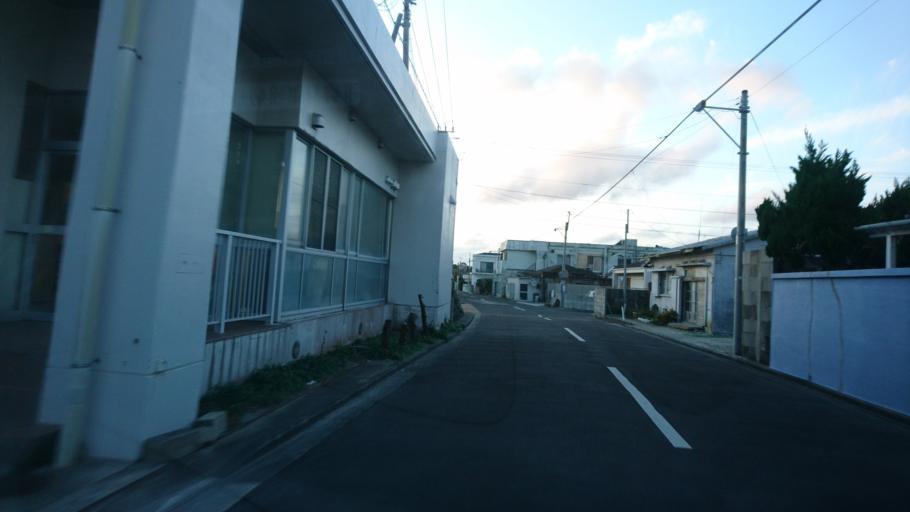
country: JP
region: Shizuoka
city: Shimoda
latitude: 34.3726
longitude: 139.2558
